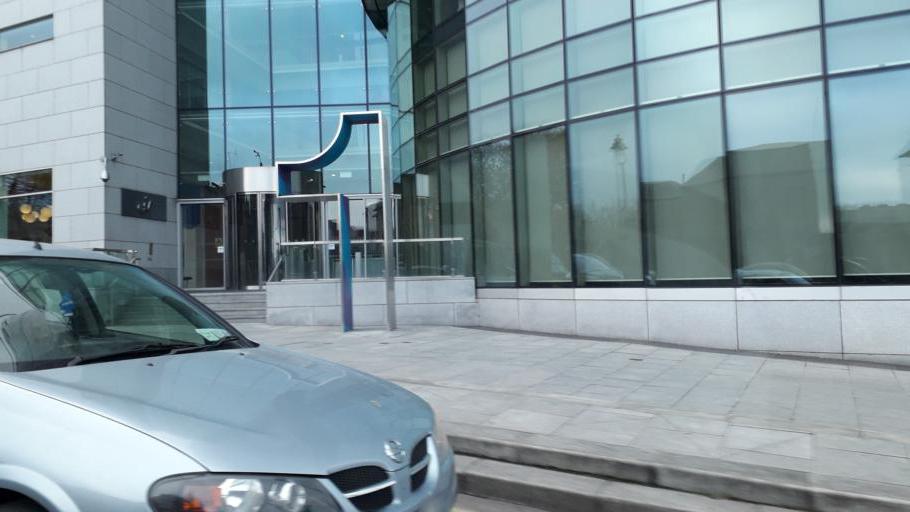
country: IE
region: Leinster
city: Rialto
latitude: 53.3457
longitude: -6.2964
